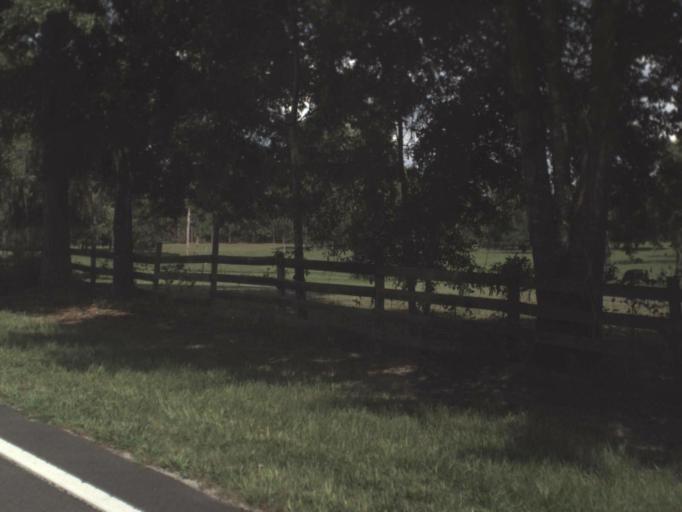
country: US
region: Florida
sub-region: Clay County
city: Keystone Heights
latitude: 29.7189
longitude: -82.0031
